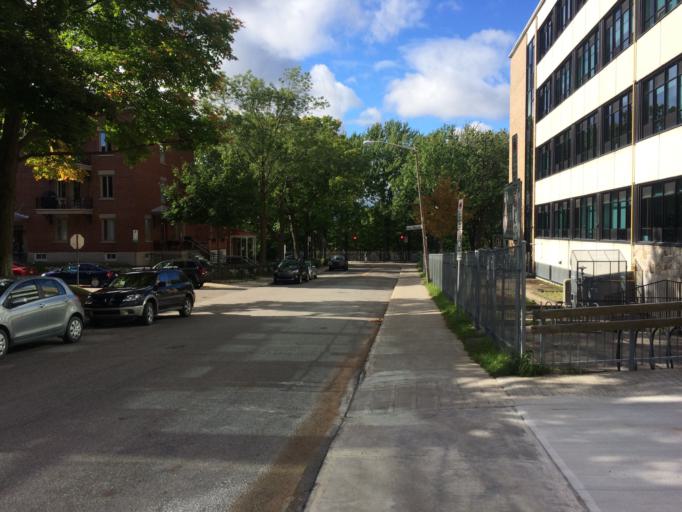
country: CA
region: Quebec
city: Quebec
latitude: 46.8015
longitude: -71.2358
